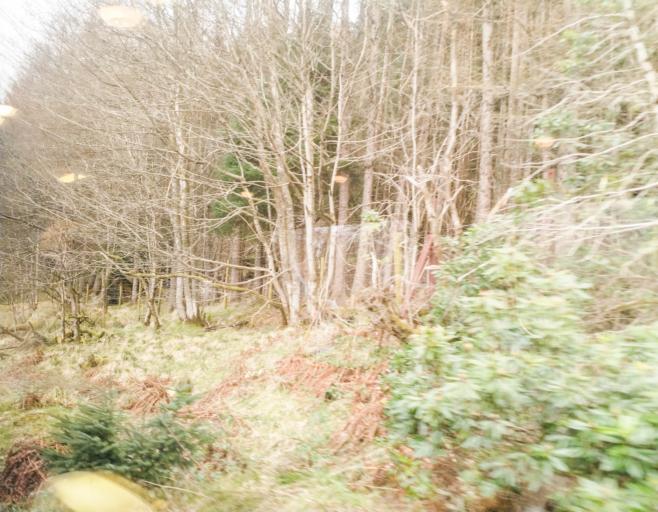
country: GB
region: Scotland
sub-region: Argyll and Bute
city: Garelochhead
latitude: 56.4355
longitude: -4.7044
